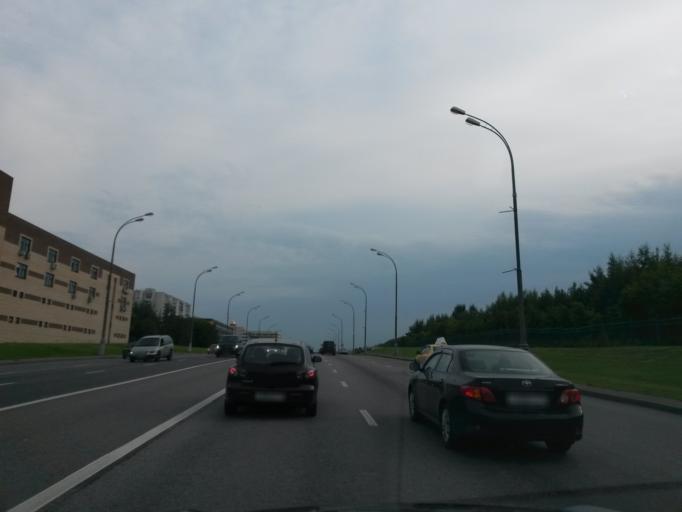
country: RU
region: Moscow
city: Chertanovo Yuzhnoye
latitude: 55.5732
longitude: 37.5635
